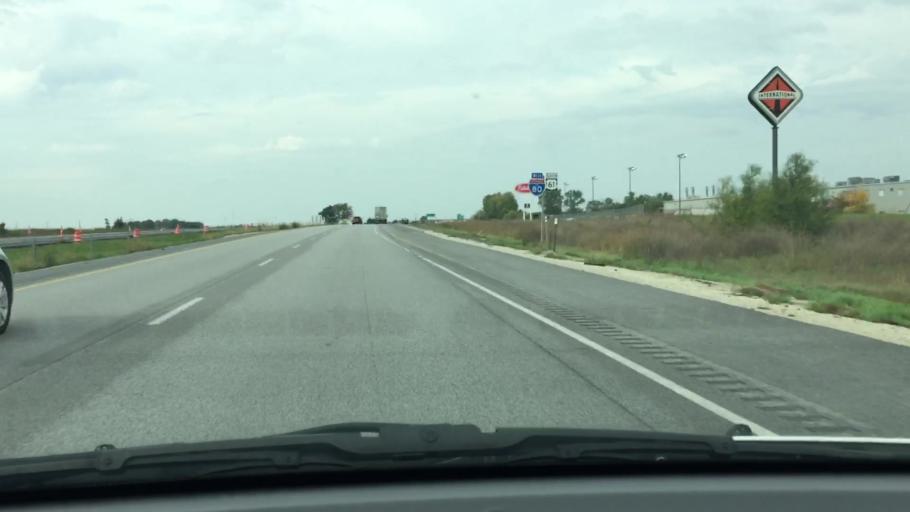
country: US
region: Iowa
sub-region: Scott County
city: Eldridge
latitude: 41.5998
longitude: -90.6276
